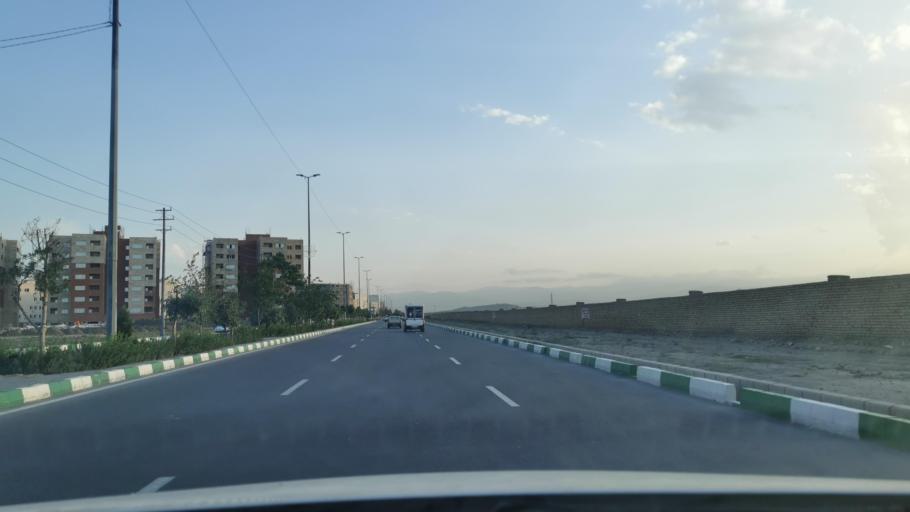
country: IR
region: Razavi Khorasan
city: Mashhad
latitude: 36.3953
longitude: 59.4741
